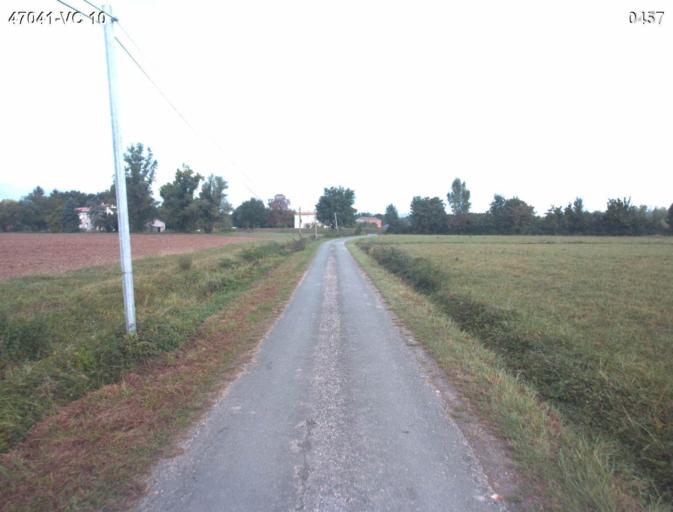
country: FR
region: Aquitaine
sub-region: Departement du Lot-et-Garonne
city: Port-Sainte-Marie
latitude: 44.2168
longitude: 0.4275
